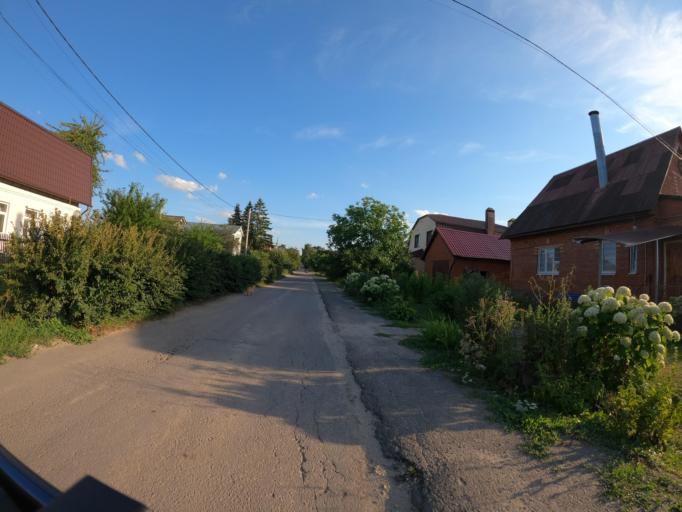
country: RU
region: Moskovskaya
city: Raduzhnyy
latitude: 55.1124
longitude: 38.7325
